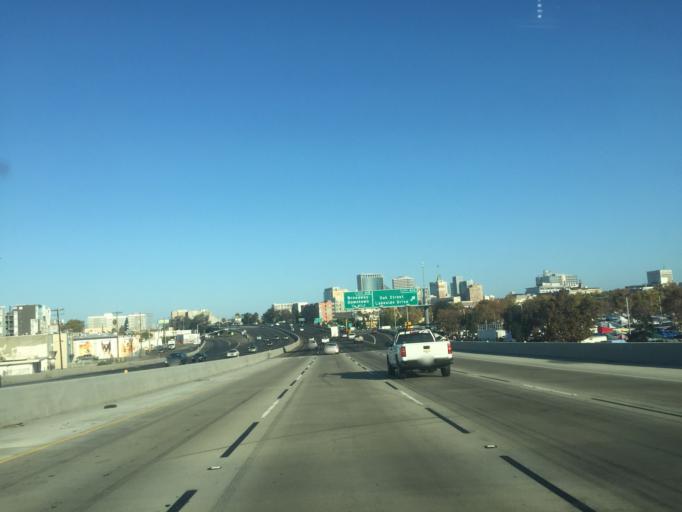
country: US
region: California
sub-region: Alameda County
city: Oakland
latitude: 37.7926
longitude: -122.2627
